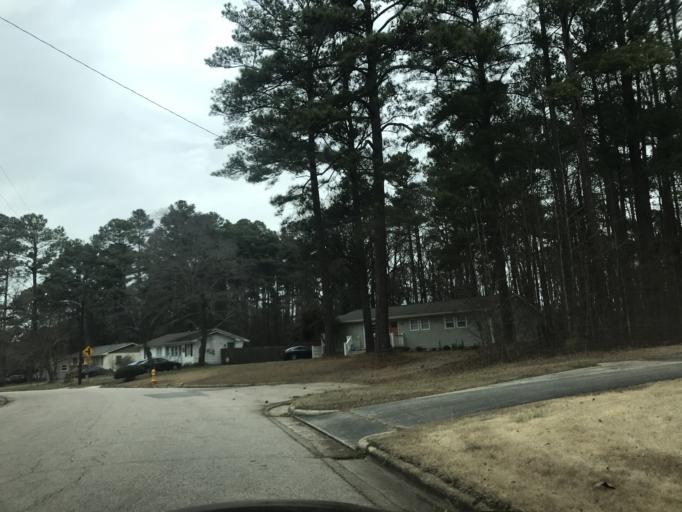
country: US
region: North Carolina
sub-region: Wake County
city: Raleigh
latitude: 35.7898
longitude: -78.5969
